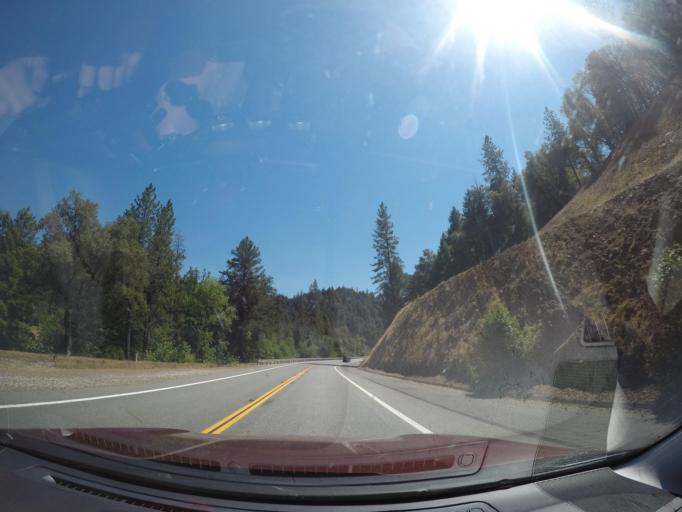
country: US
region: California
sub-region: Shasta County
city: Bella Vista
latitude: 40.7640
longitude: -122.0119
